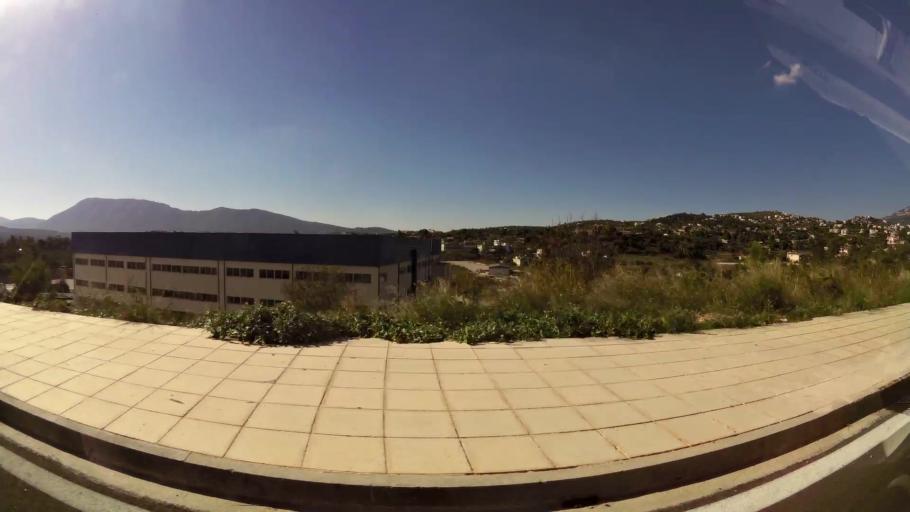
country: GR
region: Attica
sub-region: Nomarchia Anatolikis Attikis
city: Dhrafi
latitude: 38.0040
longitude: 23.9132
